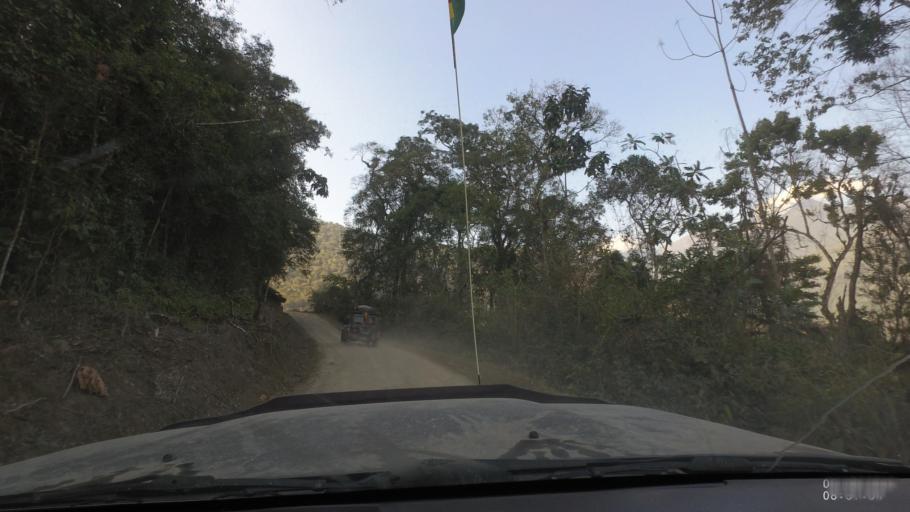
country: BO
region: La Paz
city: Quime
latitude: -16.5034
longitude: -66.7632
